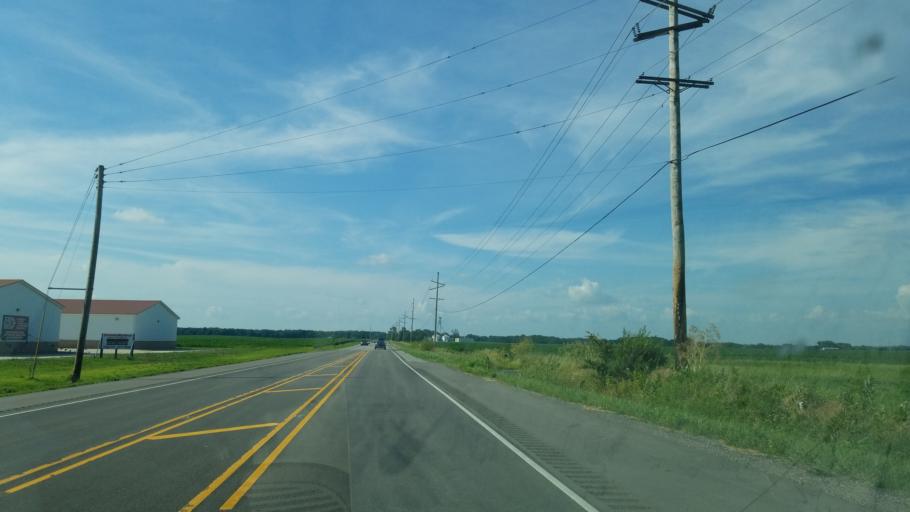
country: US
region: Illinois
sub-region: Saint Clair County
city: Scott Air Force Base
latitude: 38.5569
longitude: -89.8072
